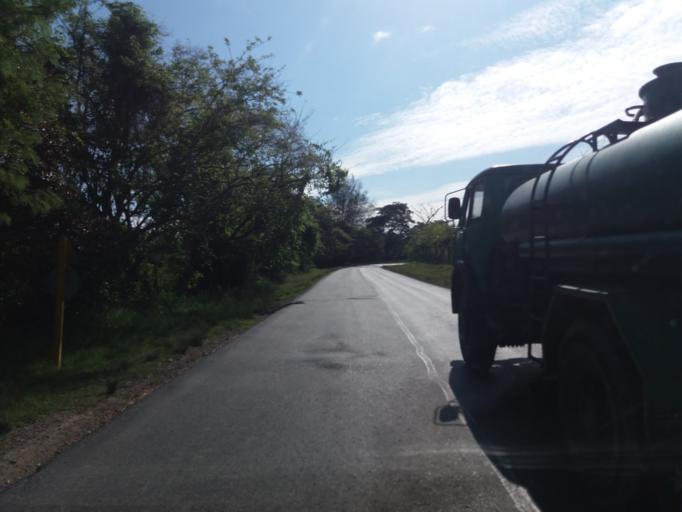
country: CU
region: Cienfuegos
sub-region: Municipio de Cienfuegos
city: Cienfuegos
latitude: 22.1605
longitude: -80.3615
